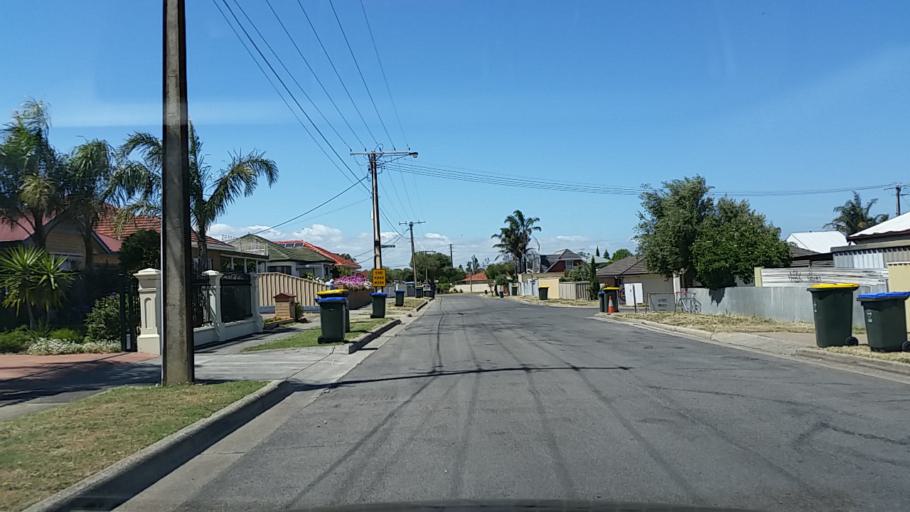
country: AU
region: South Australia
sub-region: Charles Sturt
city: Seaton
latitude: -34.9029
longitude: 138.5240
